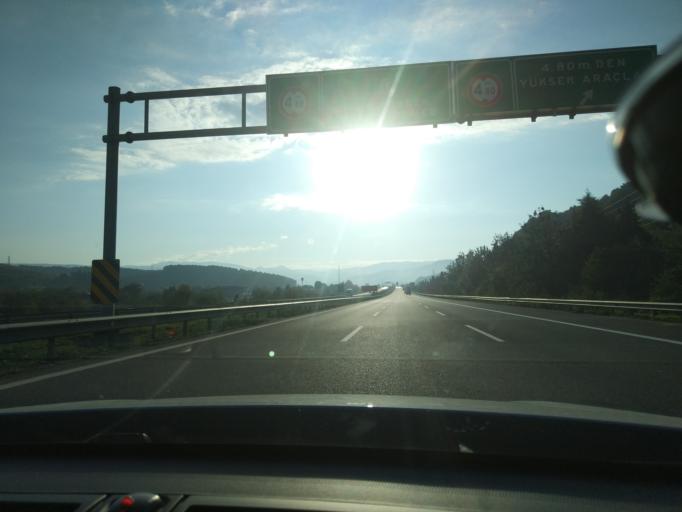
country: TR
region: Duzce
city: Kaynasli
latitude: 40.7890
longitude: 31.2531
